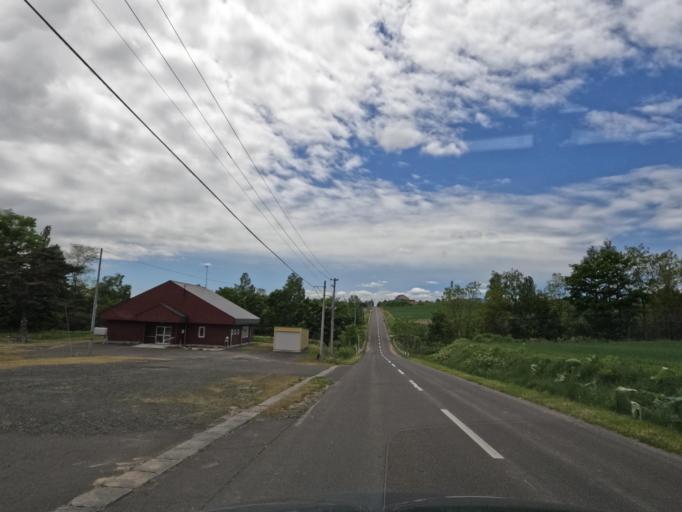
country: JP
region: Hokkaido
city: Shimo-furano
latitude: 43.5299
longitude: 142.4387
